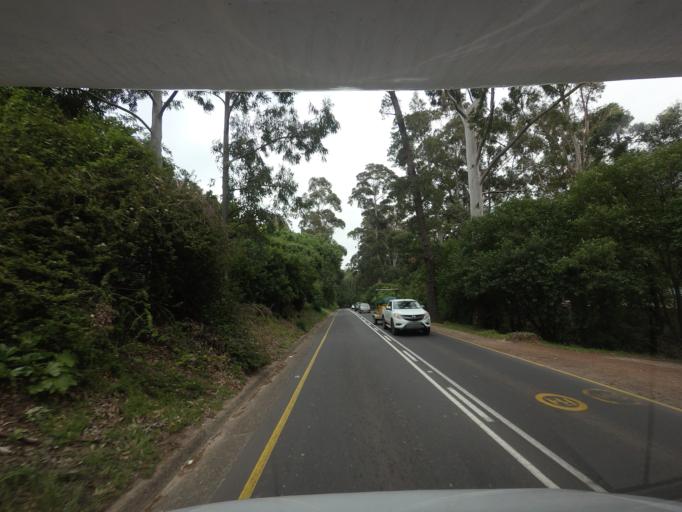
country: ZA
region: Western Cape
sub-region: City of Cape Town
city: Constantia
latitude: -34.0142
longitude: 18.3873
